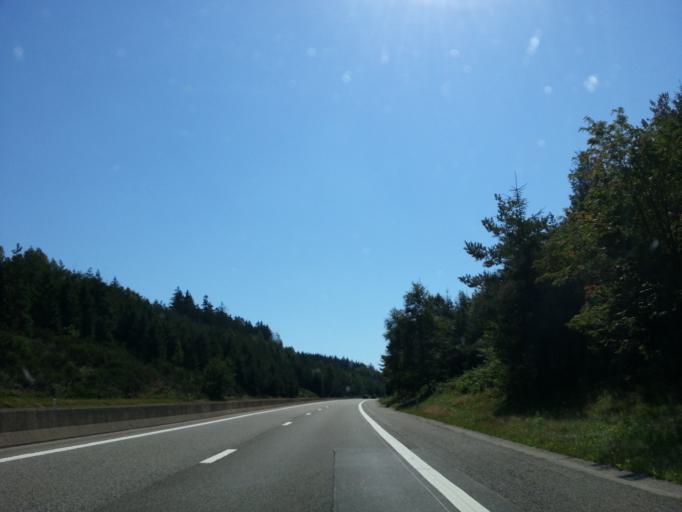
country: BE
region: Wallonia
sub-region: Province de Liege
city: Waimes
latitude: 50.3554
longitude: 6.0635
